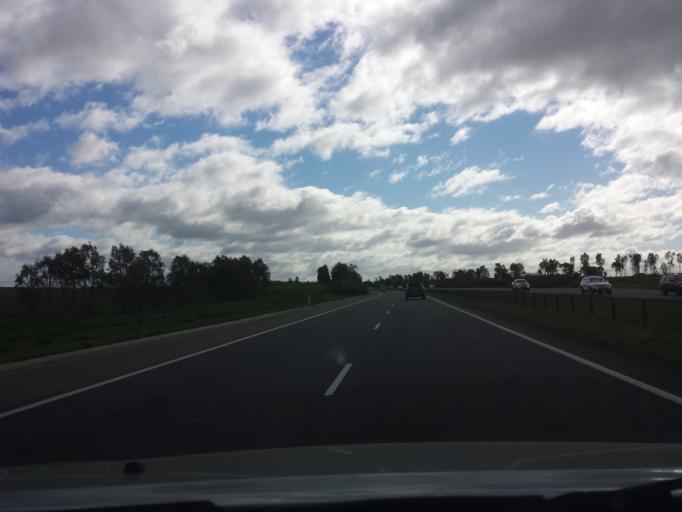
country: AU
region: Victoria
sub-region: Hume
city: Craigieburn
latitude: -37.6108
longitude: 144.9845
